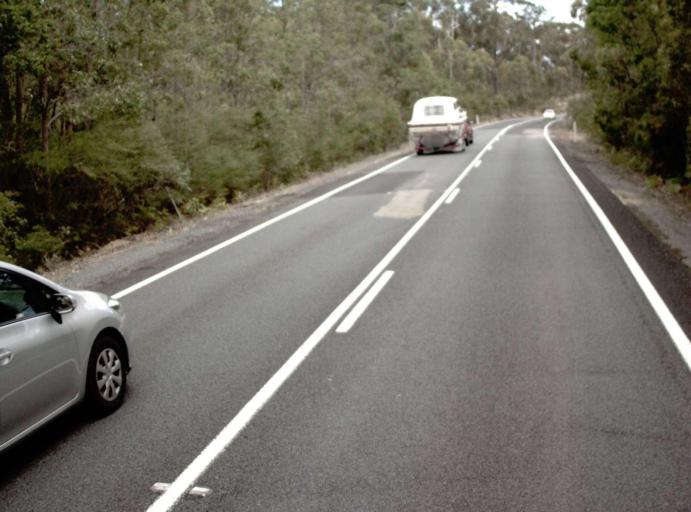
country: AU
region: New South Wales
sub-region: Bega Valley
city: Eden
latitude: -37.4904
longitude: 149.5505
